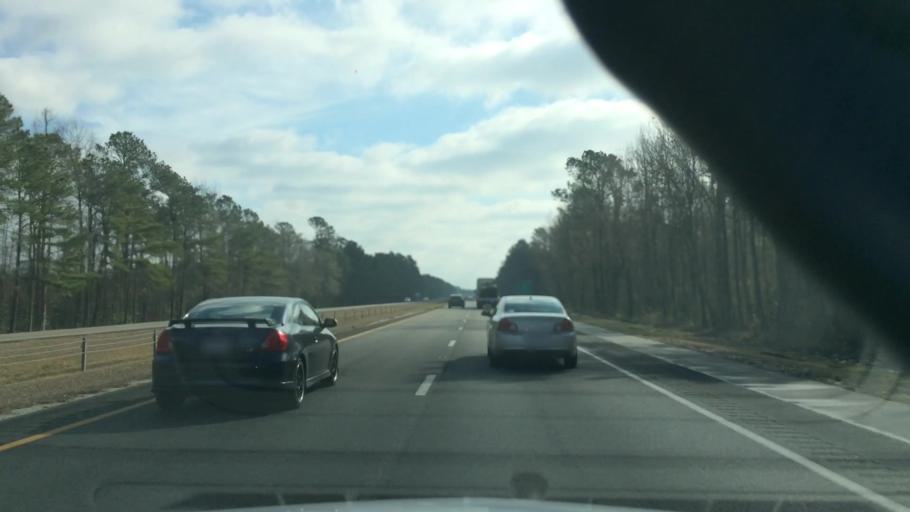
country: US
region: North Carolina
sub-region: Pender County
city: Burgaw
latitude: 34.6056
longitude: -77.9158
